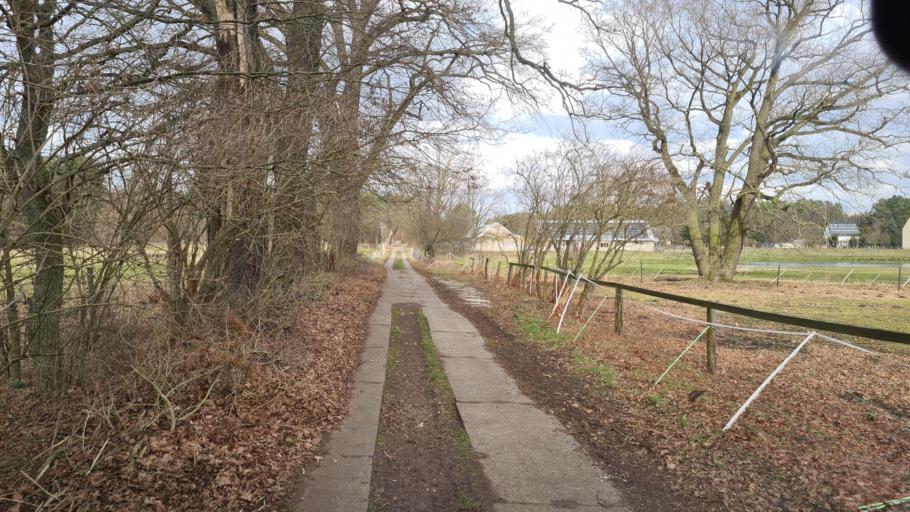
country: DE
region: Brandenburg
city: Gross Koris
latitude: 52.1479
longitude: 13.6778
